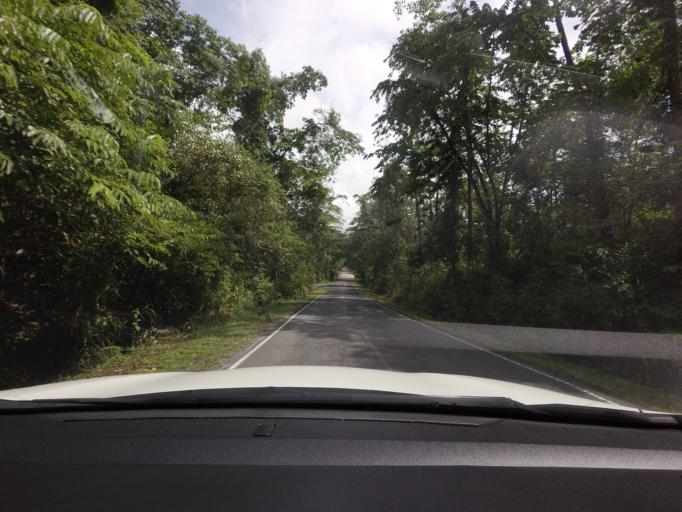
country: TH
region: Nakhon Nayok
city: Pak Phli
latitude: 14.2931
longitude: 101.3955
